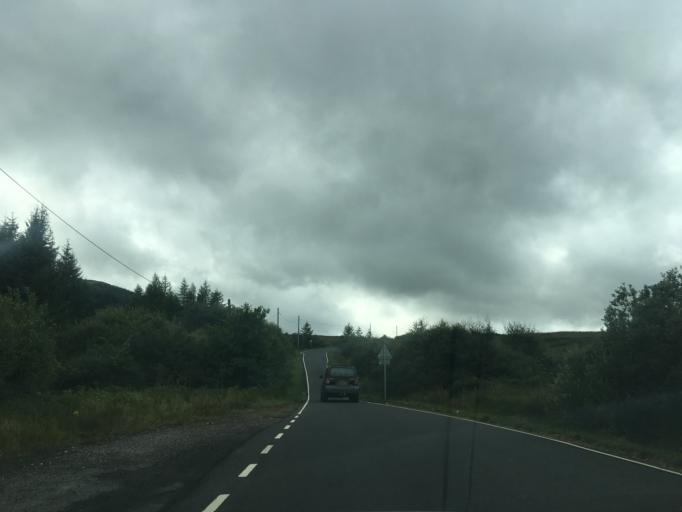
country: GB
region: Scotland
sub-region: Argyll and Bute
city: Port Bannatyne
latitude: 55.9931
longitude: -5.1361
